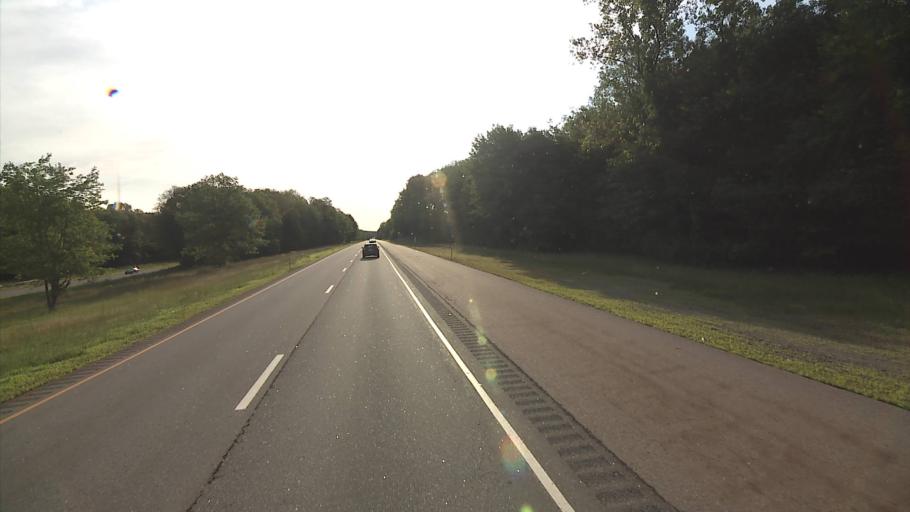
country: US
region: Connecticut
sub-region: New London County
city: Colchester
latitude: 41.5674
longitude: -72.2261
